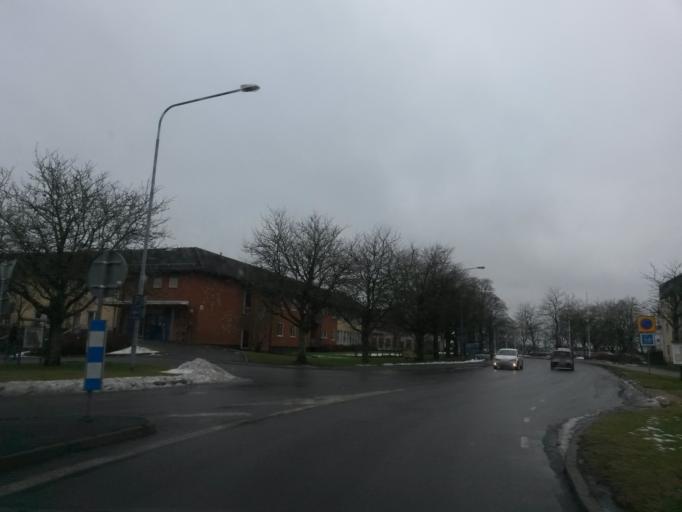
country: SE
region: Vaestra Goetaland
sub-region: Marks Kommun
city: Kinna
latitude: 57.5095
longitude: 12.6988
